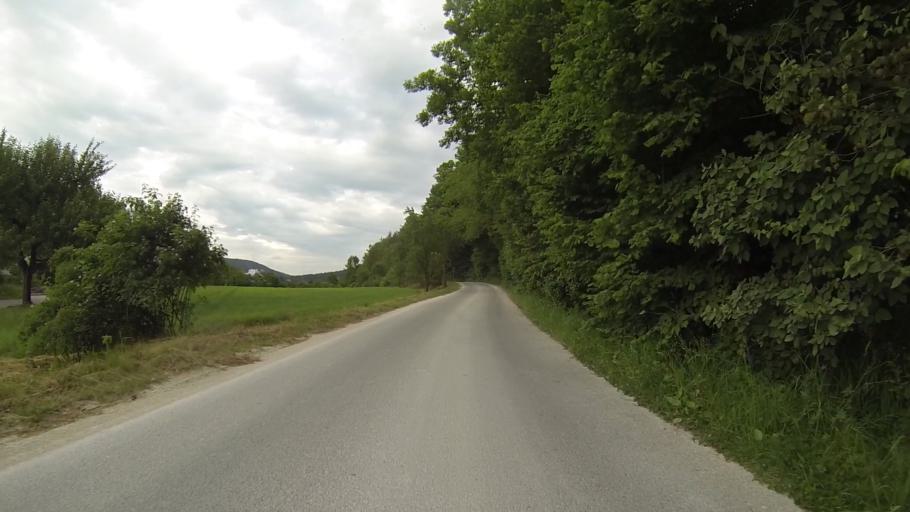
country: DE
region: Baden-Wuerttemberg
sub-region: Tuebingen Region
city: Blaubeuren
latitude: 48.3959
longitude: 9.8133
